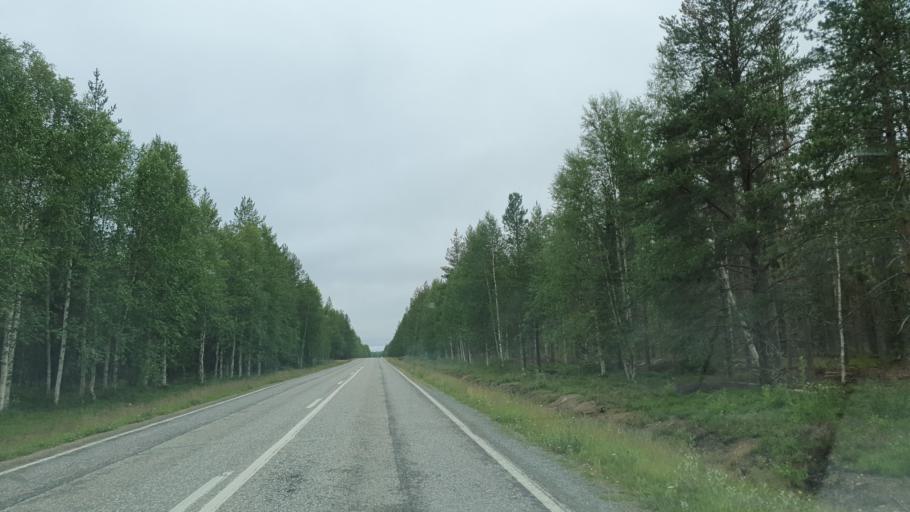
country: FI
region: Lapland
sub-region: Pohjois-Lappi
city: Sodankylae
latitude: 67.3923
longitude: 26.7595
